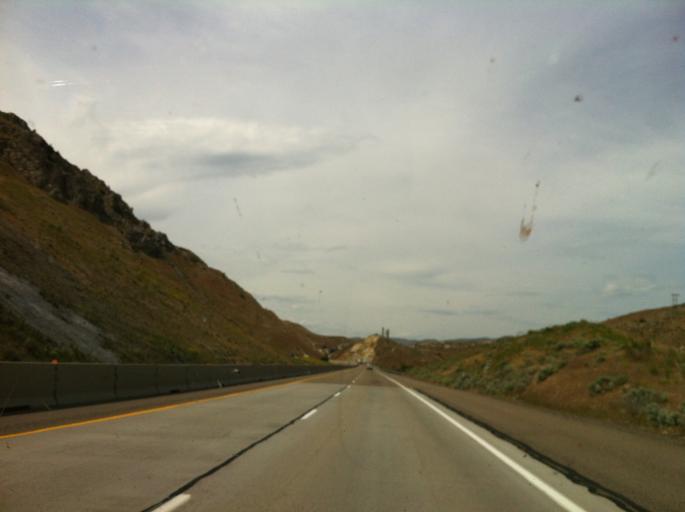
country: US
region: Idaho
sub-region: Washington County
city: Weiser
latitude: 44.3717
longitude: -117.2964
